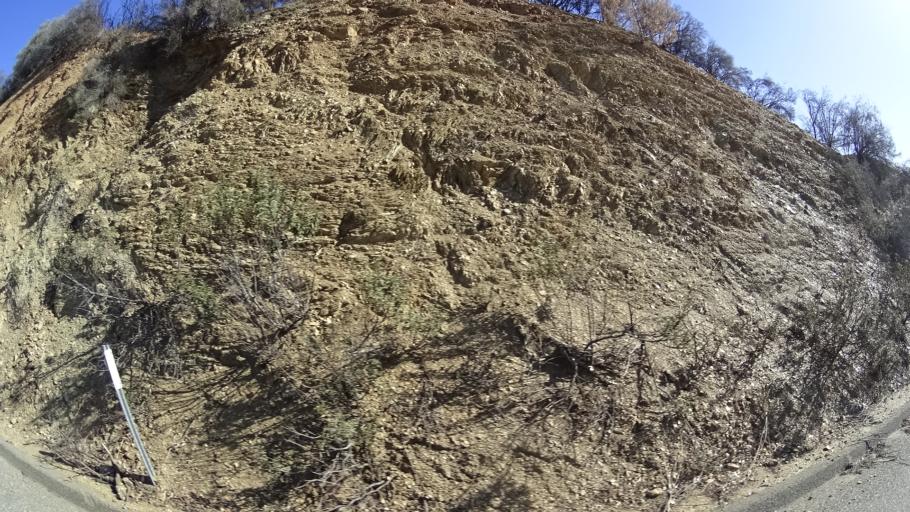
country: US
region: California
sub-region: Tehama County
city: Rancho Tehama Reserve
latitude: 39.6624
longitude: -122.6363
